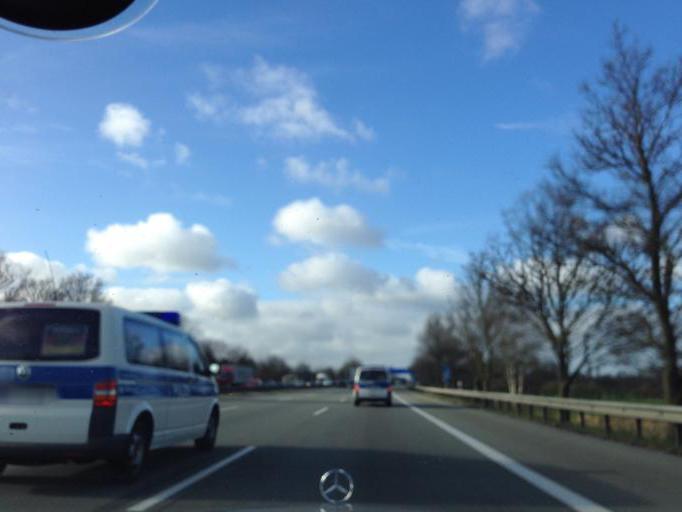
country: DE
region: Lower Saxony
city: Seevetal
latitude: 53.4007
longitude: 10.0265
